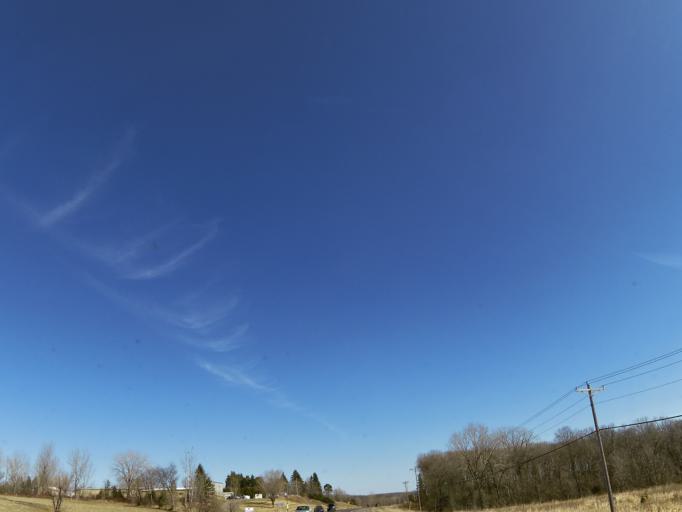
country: US
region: Minnesota
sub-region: Hennepin County
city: Medina
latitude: 45.0656
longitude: -93.6133
